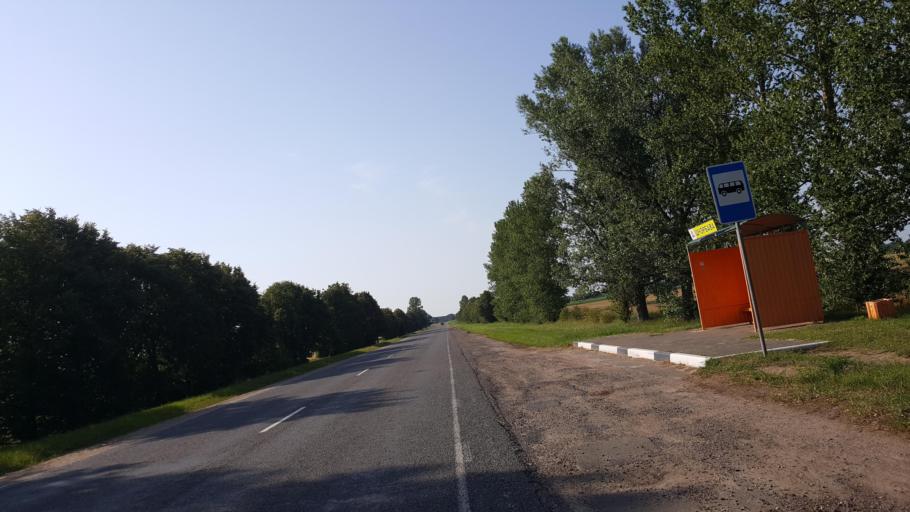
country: BY
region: Brest
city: Kamyanyets
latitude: 52.3586
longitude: 23.8935
